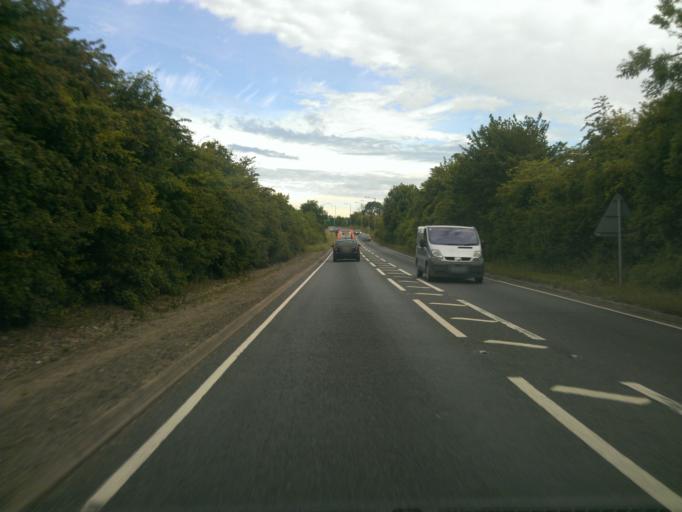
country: GB
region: England
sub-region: Essex
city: Coggeshall
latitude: 51.8769
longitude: 0.6996
